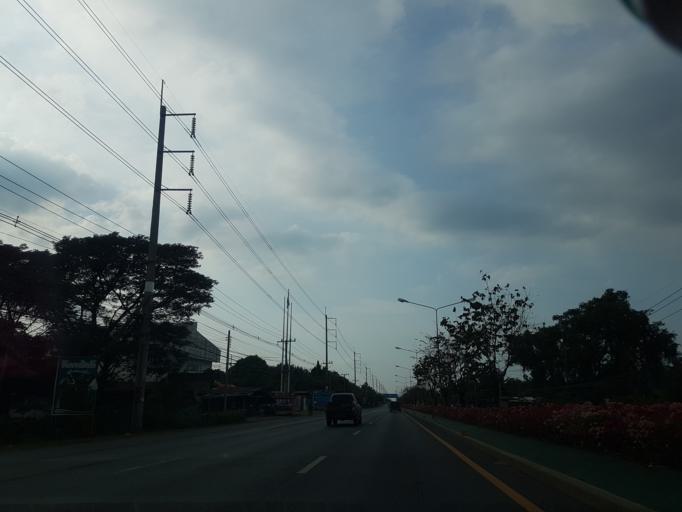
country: TH
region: Sara Buri
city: Phra Phutthabat
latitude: 14.7512
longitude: 100.7433
